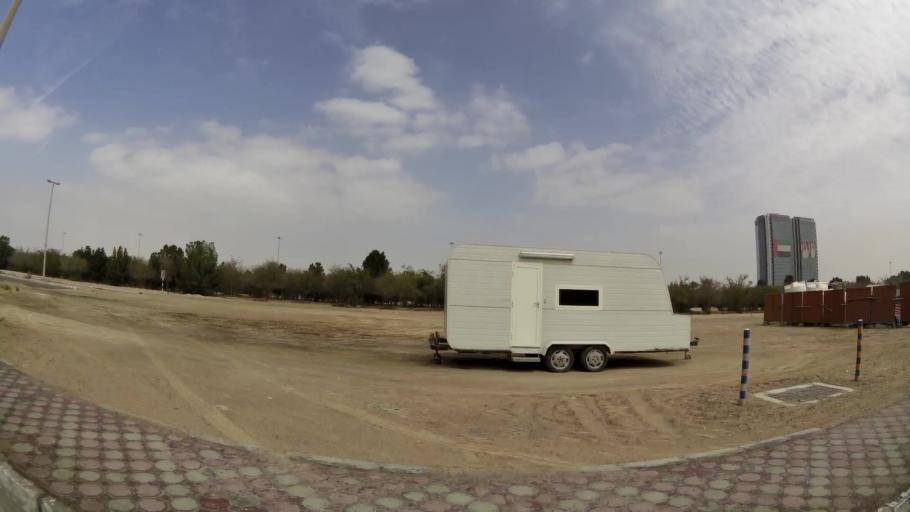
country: AE
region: Abu Dhabi
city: Abu Dhabi
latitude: 24.3937
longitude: 54.5137
